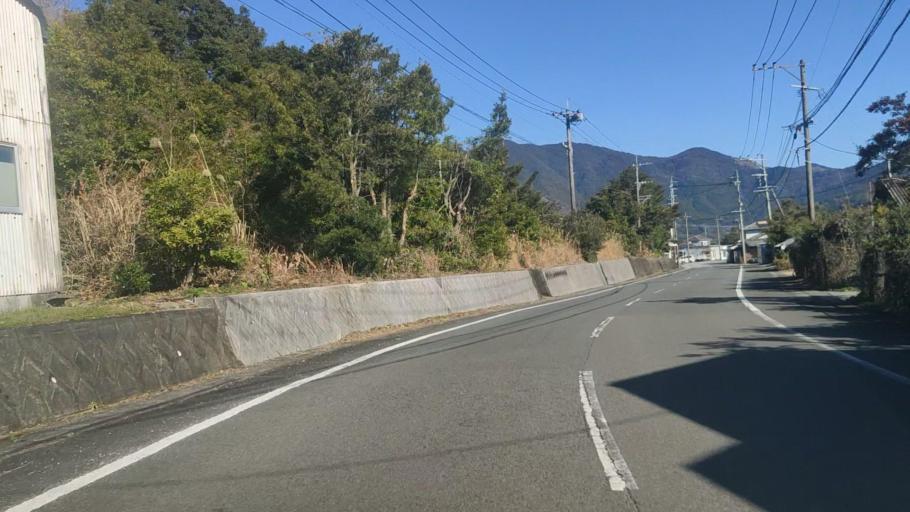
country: JP
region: Oita
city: Saiki
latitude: 32.8033
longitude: 131.8881
